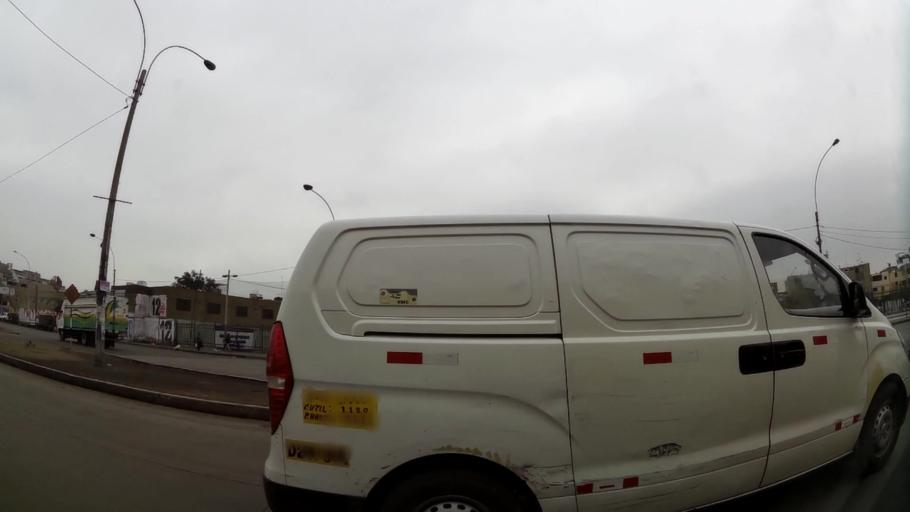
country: PE
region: Lima
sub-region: Lima
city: San Luis
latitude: -12.0576
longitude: -77.0074
